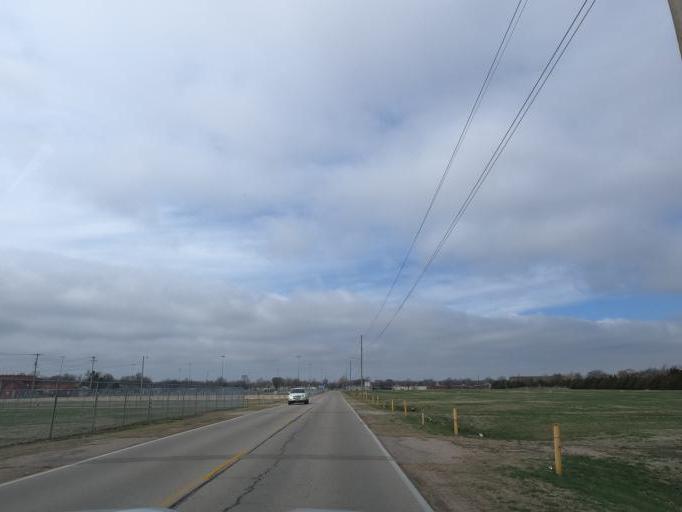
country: US
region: Kansas
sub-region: Reno County
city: Hutchinson
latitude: 38.0811
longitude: -97.9251
